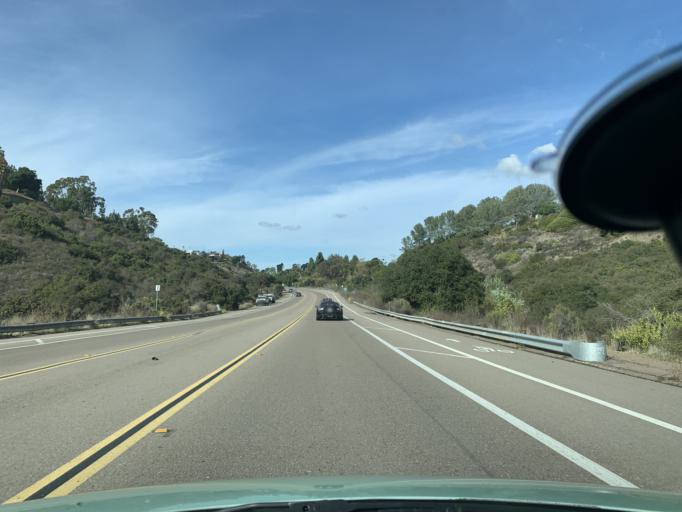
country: US
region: California
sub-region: San Diego County
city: San Diego
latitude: 32.8017
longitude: -117.1737
